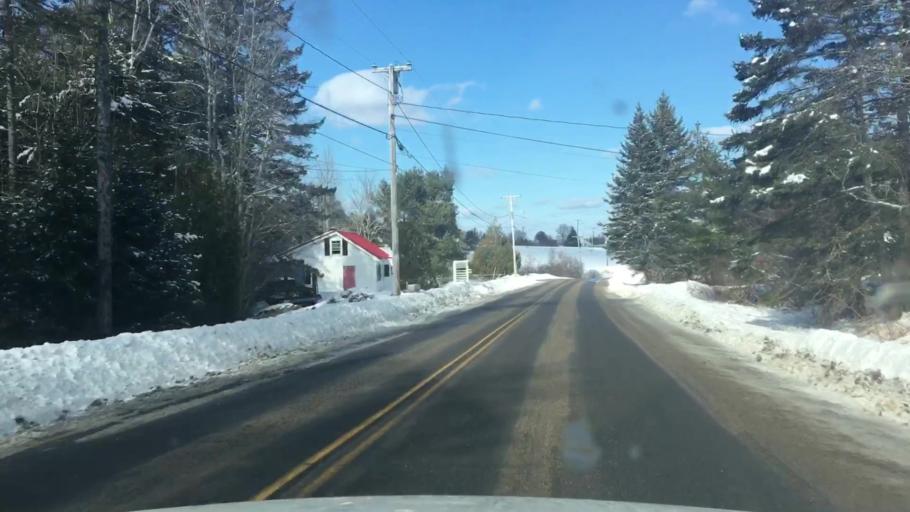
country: US
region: Maine
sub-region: Washington County
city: Machias
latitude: 44.6940
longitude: -67.4675
